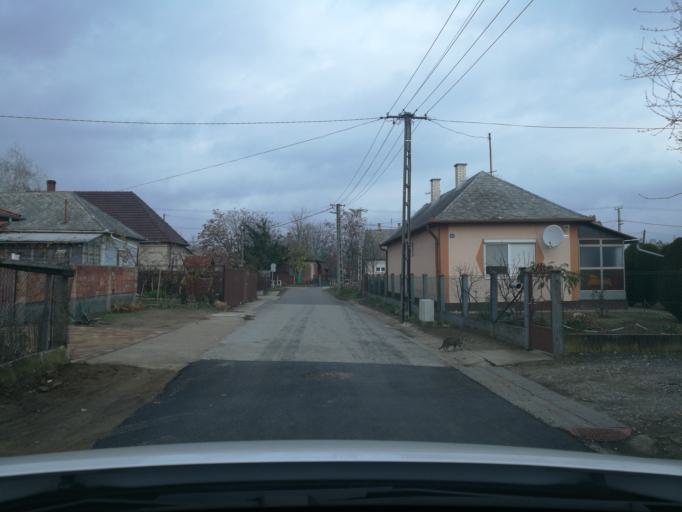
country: HU
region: Szabolcs-Szatmar-Bereg
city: Nyirpazony
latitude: 47.9592
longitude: 21.7978
